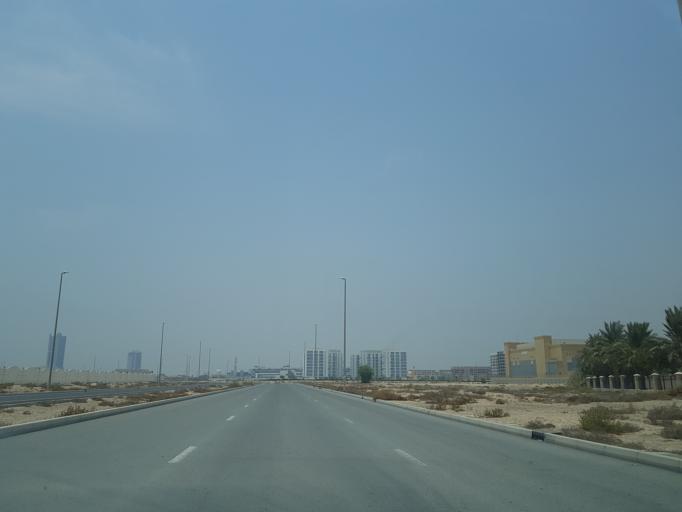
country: AE
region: Dubai
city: Dubai
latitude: 25.0352
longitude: 55.2478
